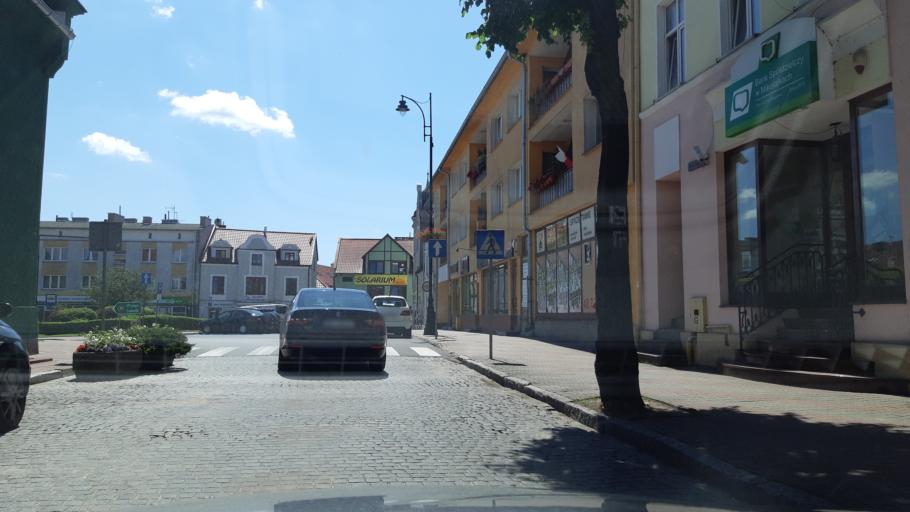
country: PL
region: Warmian-Masurian Voivodeship
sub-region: Powiat mragowski
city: Mragowo
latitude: 53.8705
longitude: 21.3034
